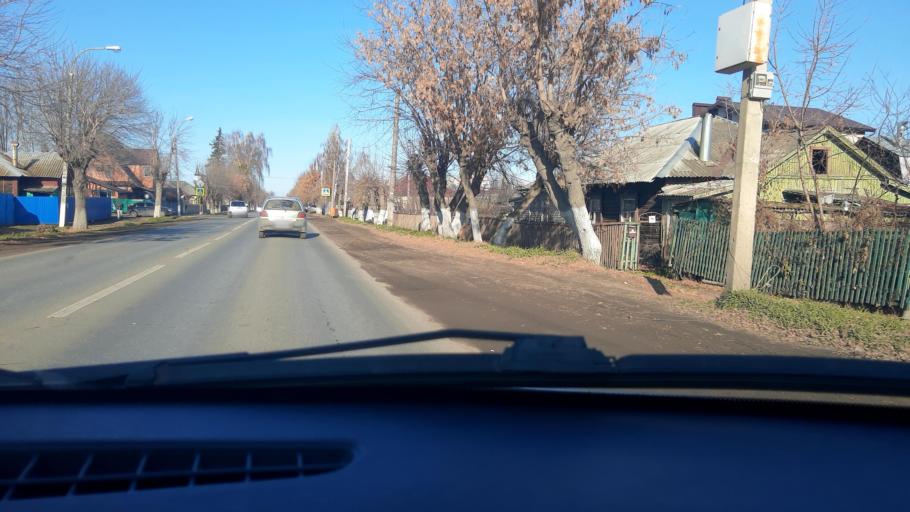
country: RU
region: Bashkortostan
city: Avdon
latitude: 54.7020
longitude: 55.8221
